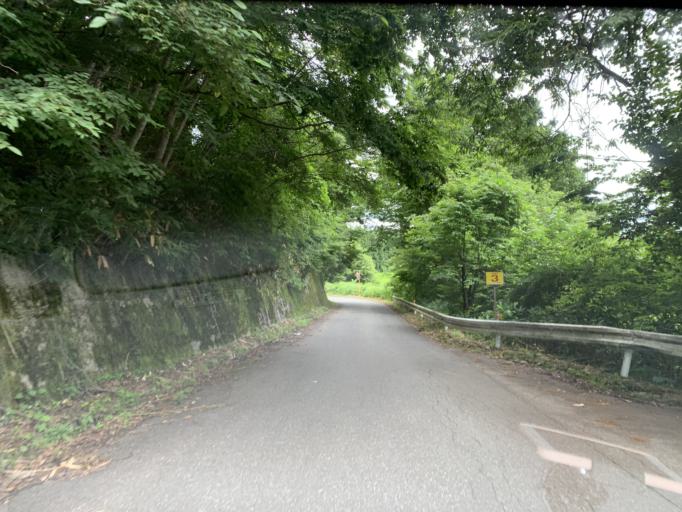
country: JP
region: Iwate
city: Ichinoseki
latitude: 38.9703
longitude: 140.9285
